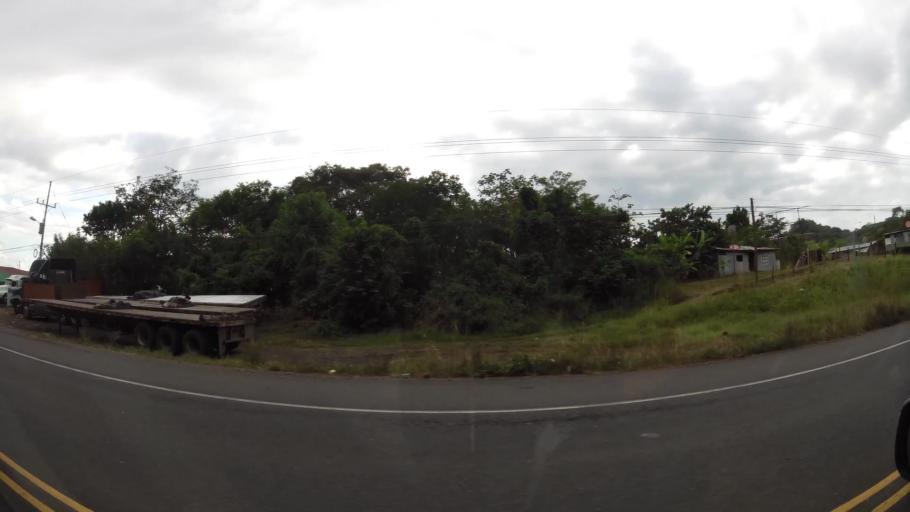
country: CR
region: Puntarenas
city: Esparza
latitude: 9.9158
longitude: -84.6825
